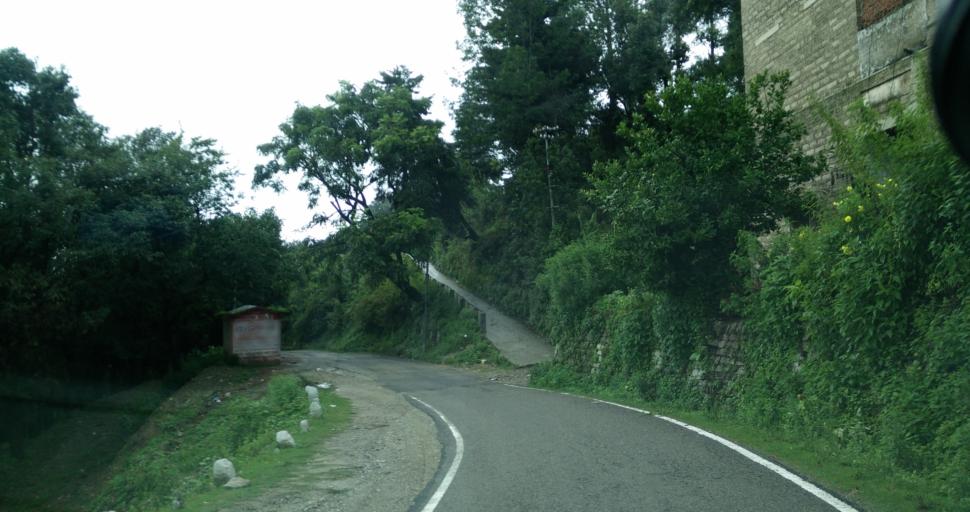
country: IN
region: Uttarakhand
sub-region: Garhwal
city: Lansdowne
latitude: 29.8621
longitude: 78.6815
